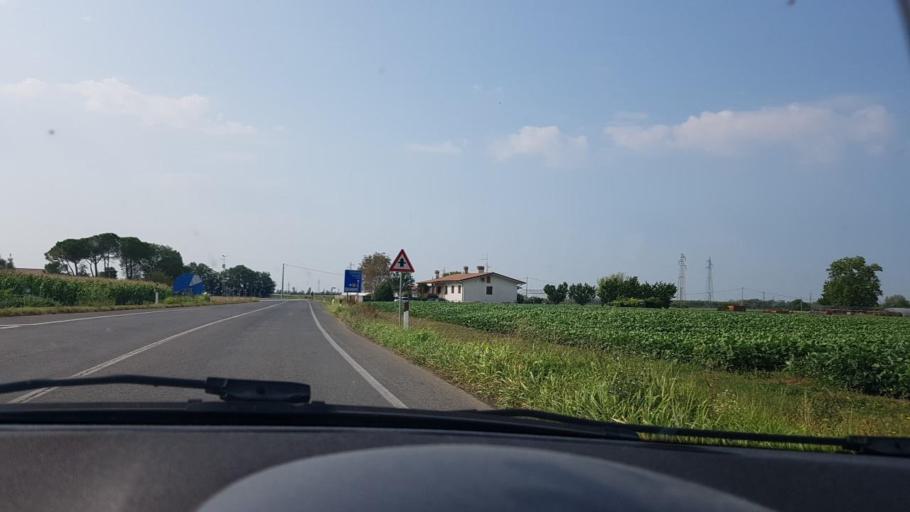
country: IT
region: Friuli Venezia Giulia
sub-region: Provincia di Gorizia
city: Romans d'Isonzo
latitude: 45.8874
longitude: 13.4327
